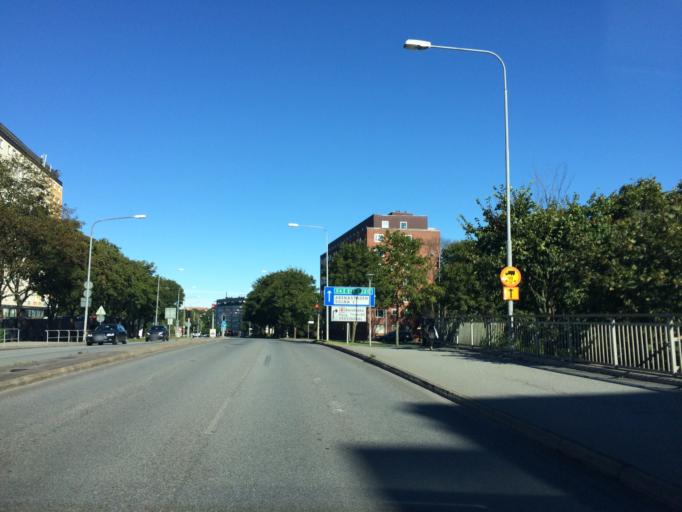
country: SE
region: Stockholm
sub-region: Solna Kommun
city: Solna
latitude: 59.3548
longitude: 17.9974
